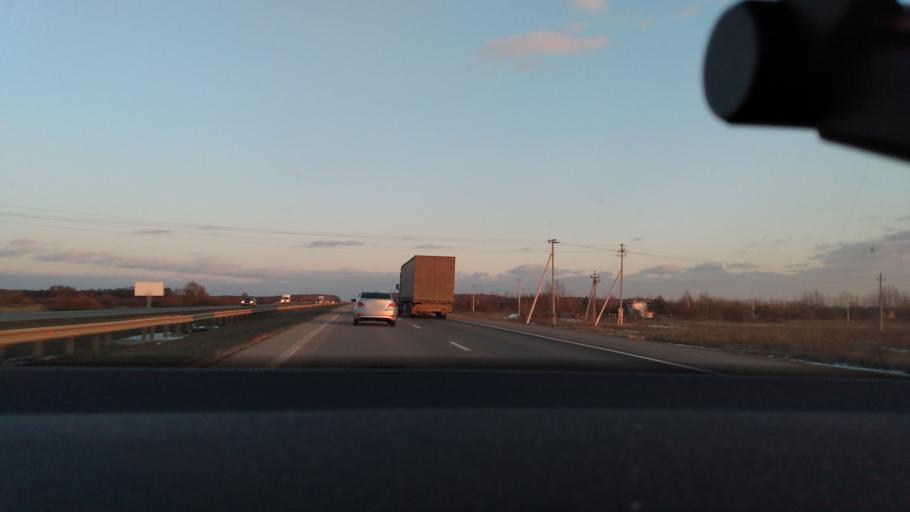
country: RU
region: Moskovskaya
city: Kolomna
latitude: 55.1132
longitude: 38.8568
